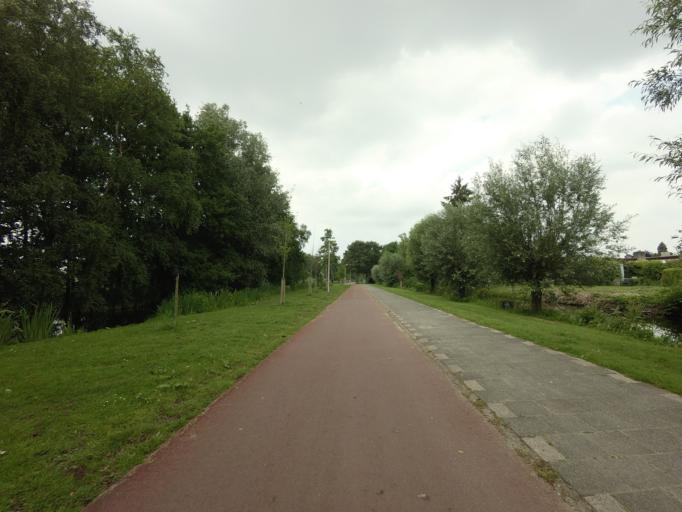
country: NL
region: South Holland
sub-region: Gemeente Krimpen aan den IJssel
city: Krimpen aan den IJssel
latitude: 51.9169
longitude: 4.6099
